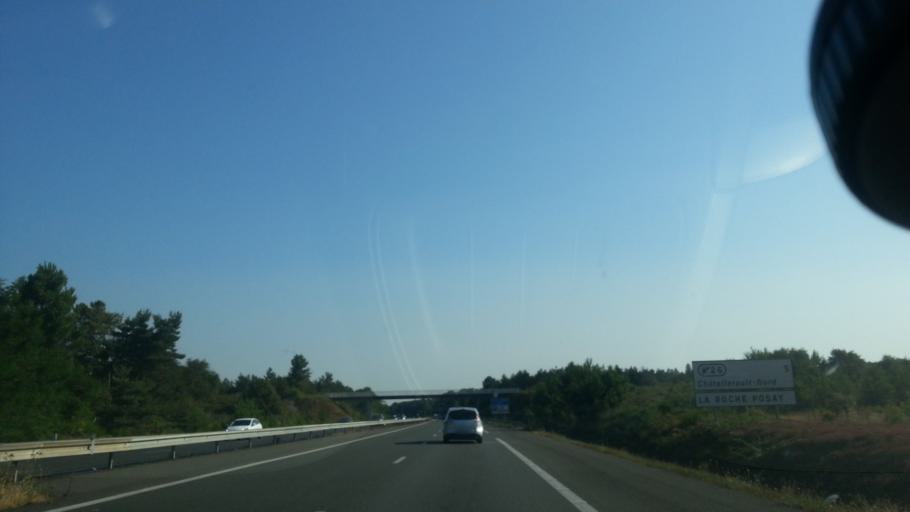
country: FR
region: Poitou-Charentes
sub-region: Departement de la Vienne
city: Naintre
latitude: 46.7868
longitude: 0.5060
